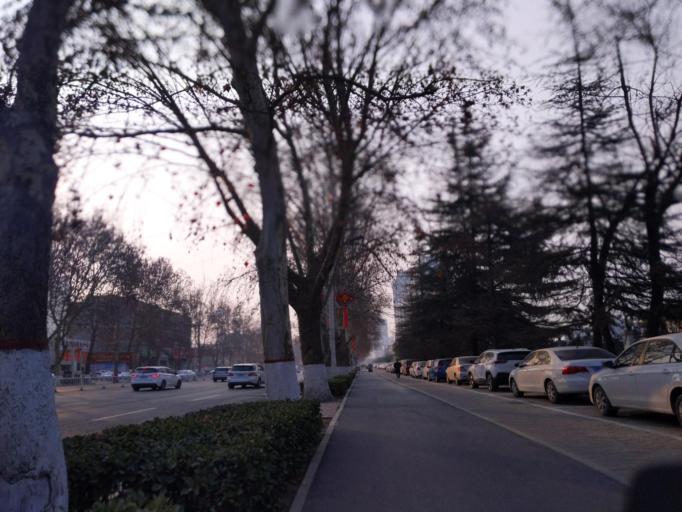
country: CN
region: Henan Sheng
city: Zhongyuanlu
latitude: 35.7788
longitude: 115.0578
